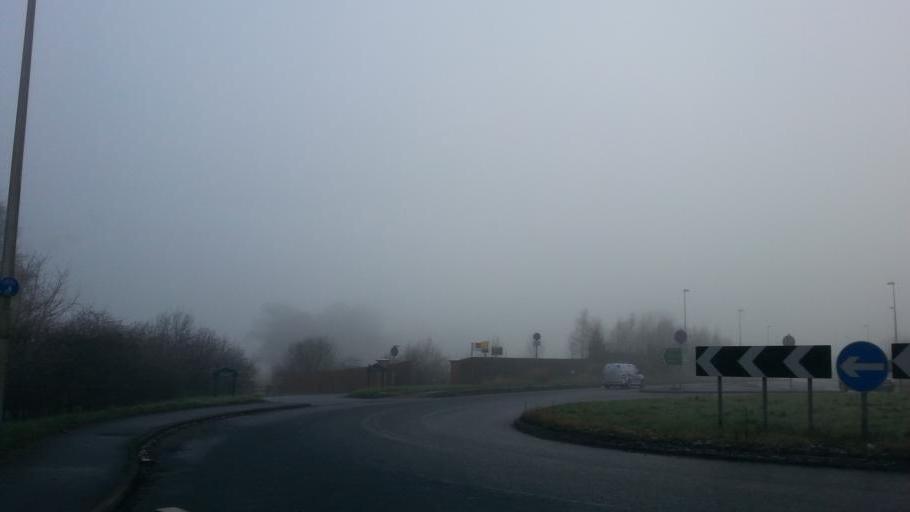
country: GB
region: England
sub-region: Cheshire East
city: Alderley Edge
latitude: 53.2734
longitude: -2.2399
